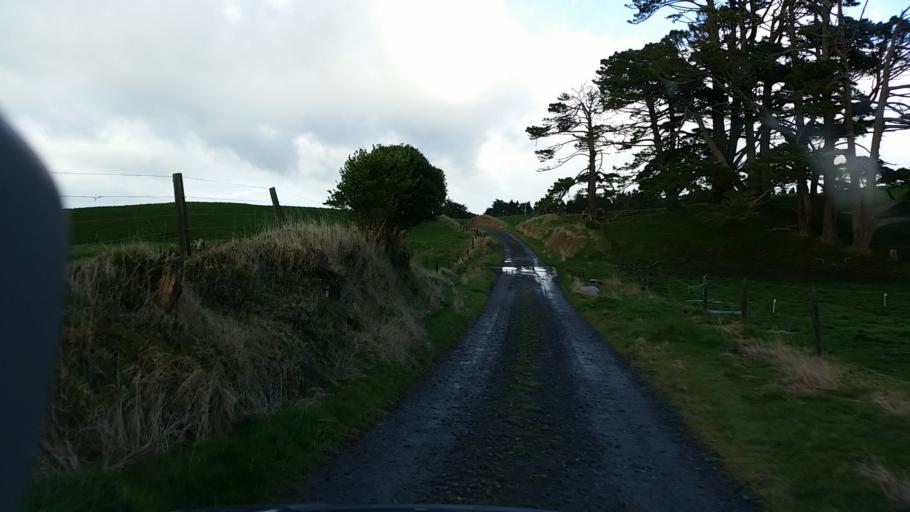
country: NZ
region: Taranaki
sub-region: South Taranaki District
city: Eltham
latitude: -39.3300
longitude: 174.1731
